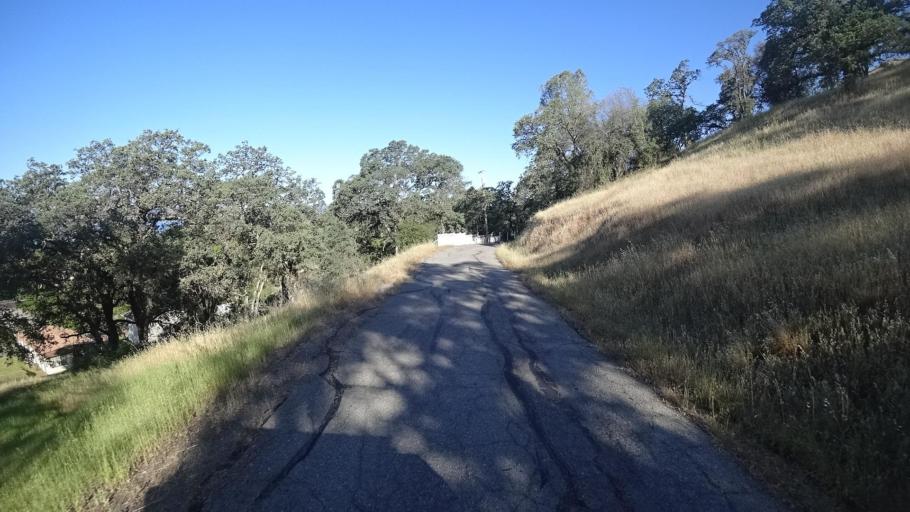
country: US
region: California
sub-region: Lake County
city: Nice
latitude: 39.1217
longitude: -122.8357
